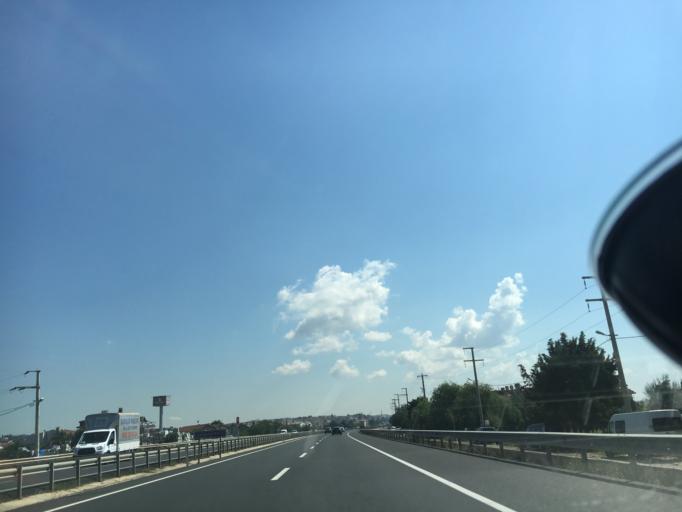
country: TR
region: Istanbul
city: Canta
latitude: 41.0552
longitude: 28.0668
